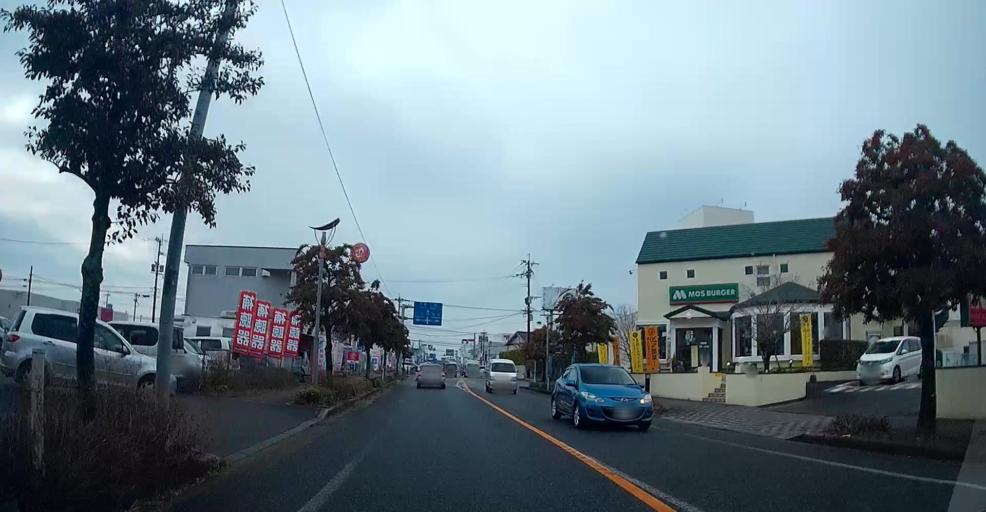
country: JP
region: Kumamoto
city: Matsubase
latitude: 32.6531
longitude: 130.6770
